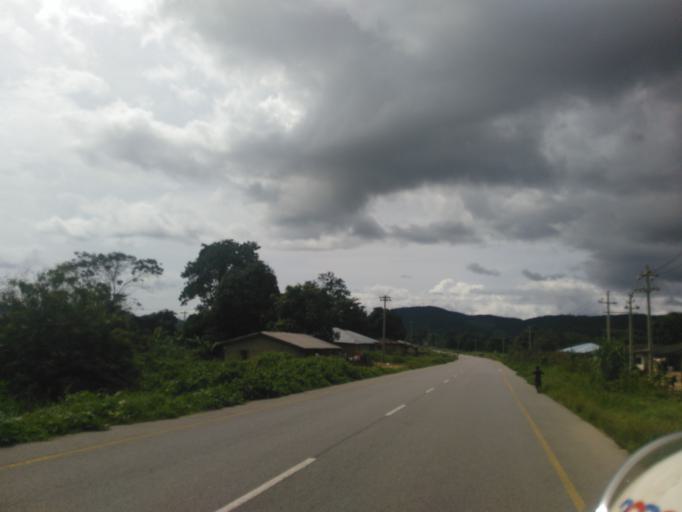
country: SL
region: Northern Province
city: Makali
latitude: 8.6260
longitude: -11.6557
